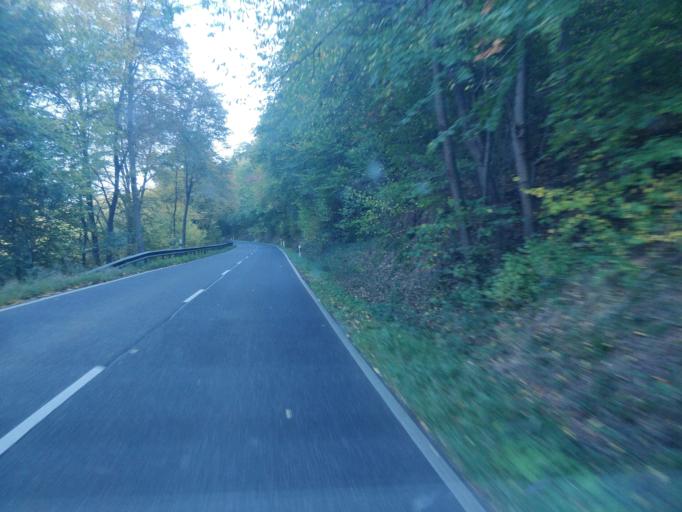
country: DE
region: North Rhine-Westphalia
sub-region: Regierungsbezirk Koln
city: Bad Munstereifel
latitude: 50.5599
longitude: 6.7813
